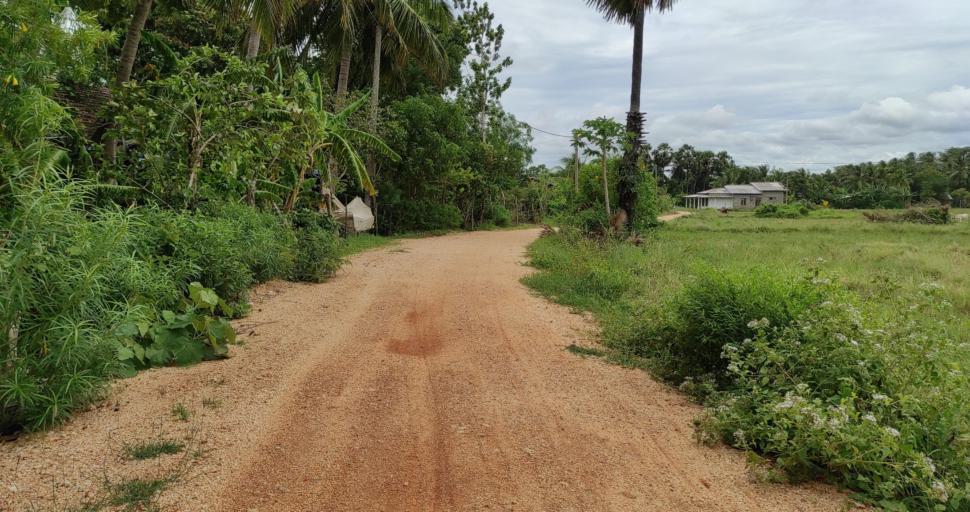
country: LK
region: Eastern Province
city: Trincomalee
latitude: 8.4458
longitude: 81.0519
